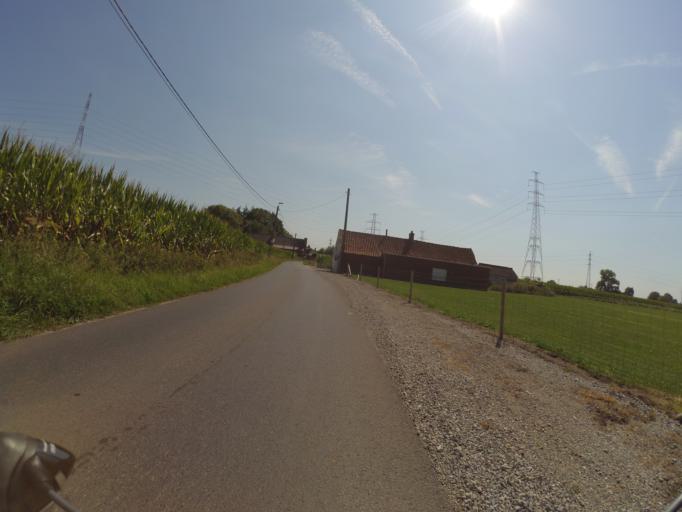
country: BE
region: Flanders
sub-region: Provincie West-Vlaanderen
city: Avelgem
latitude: 50.7874
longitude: 3.4666
